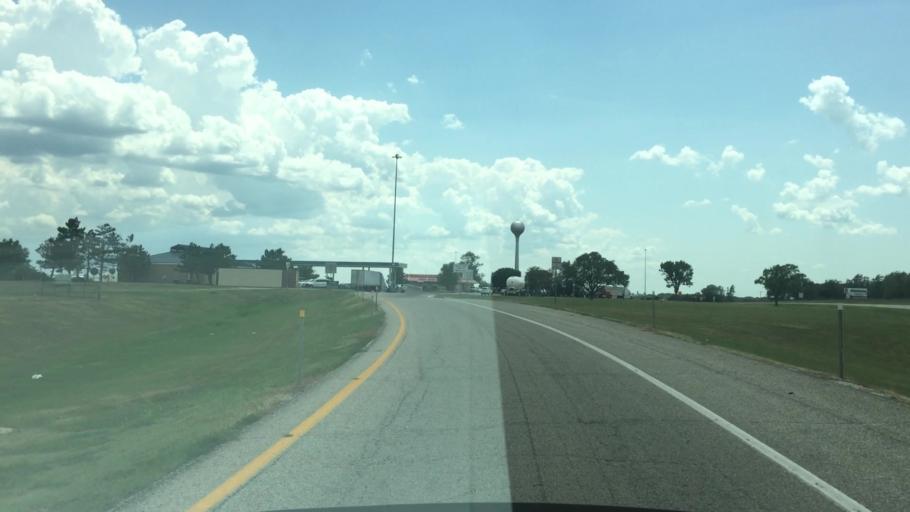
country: US
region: Kansas
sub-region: Lyon County
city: Emporia
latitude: 38.4731
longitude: -96.1842
